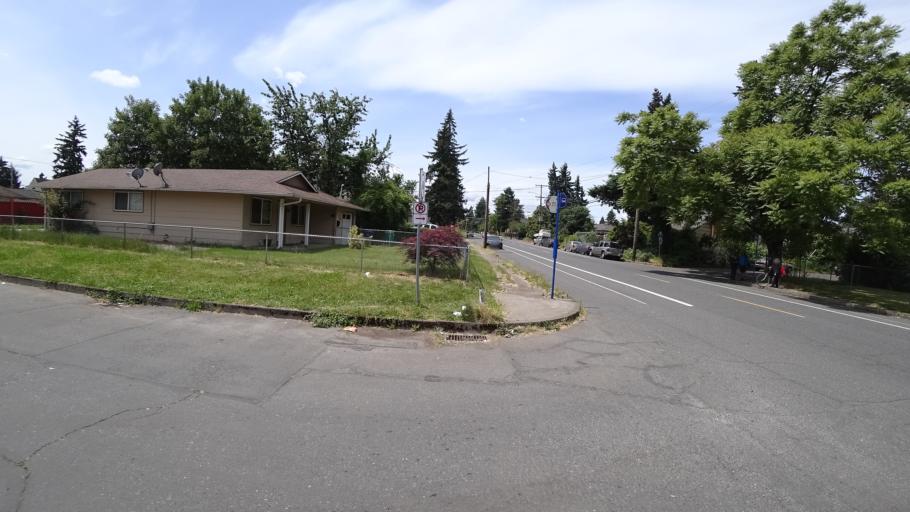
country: US
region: Oregon
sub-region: Multnomah County
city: Lents
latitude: 45.4685
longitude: -122.5949
